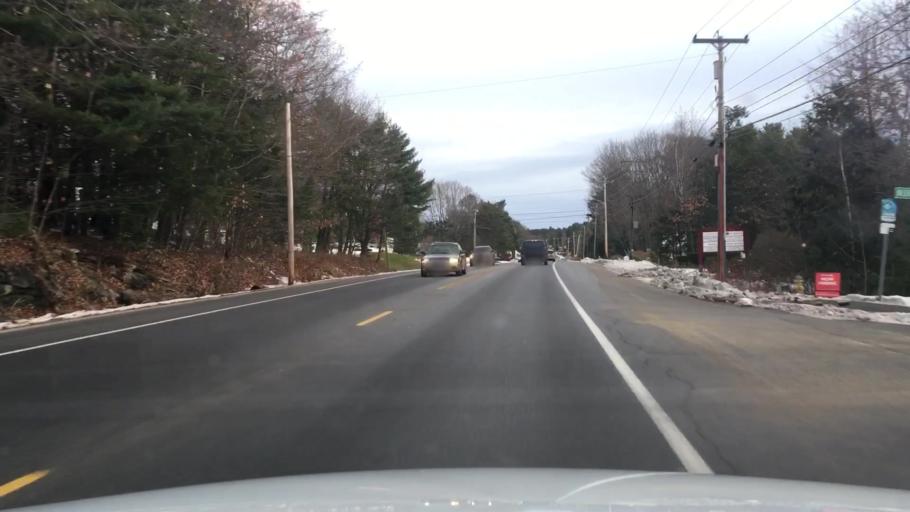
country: US
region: Maine
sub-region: Cumberland County
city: Falmouth Foreside
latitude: 43.7369
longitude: -70.2238
